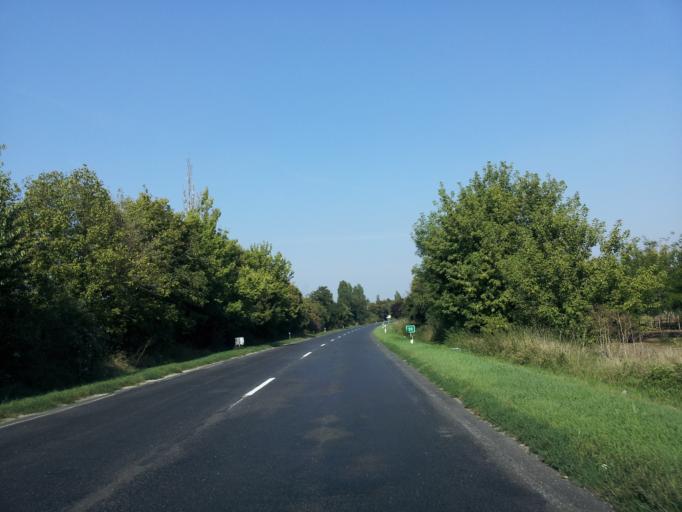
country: HU
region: Fejer
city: Lepseny
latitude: 46.9646
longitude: 18.1967
